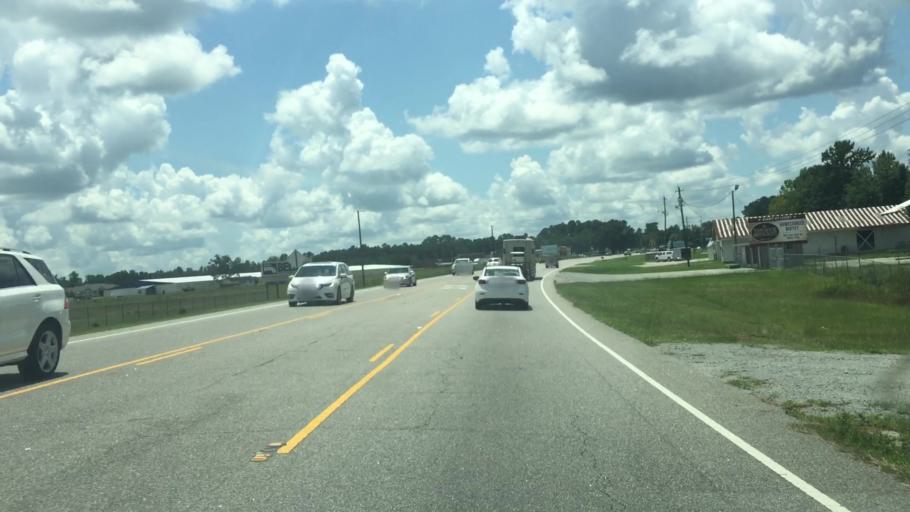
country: US
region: North Carolina
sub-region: Columbus County
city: Tabor City
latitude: 34.1440
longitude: -78.8646
